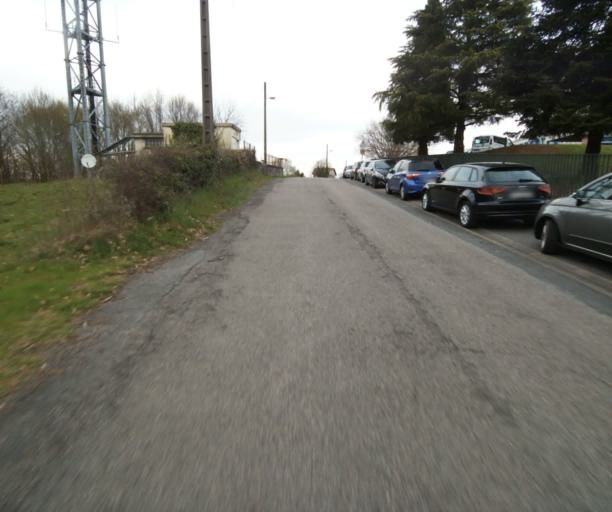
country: FR
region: Limousin
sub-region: Departement de la Correze
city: Tulle
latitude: 45.2589
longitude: 1.7662
